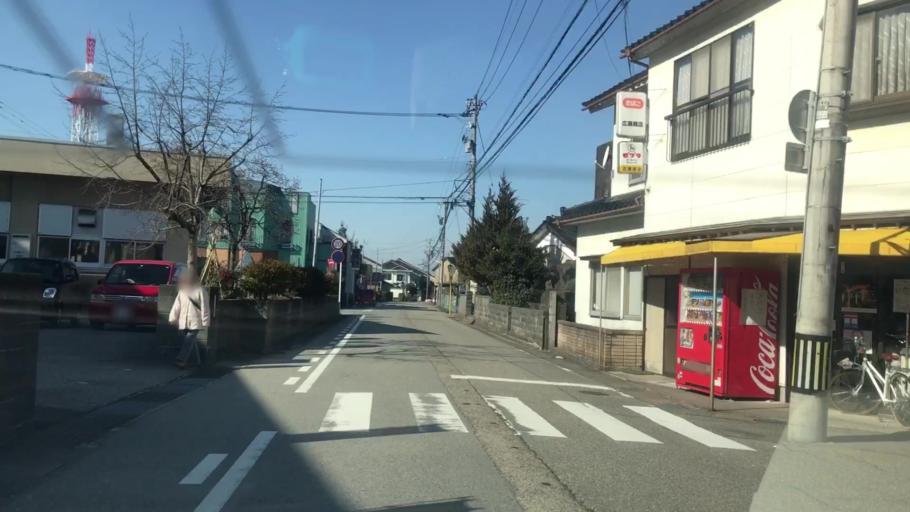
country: JP
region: Toyama
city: Toyama-shi
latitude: 36.6790
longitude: 137.2403
